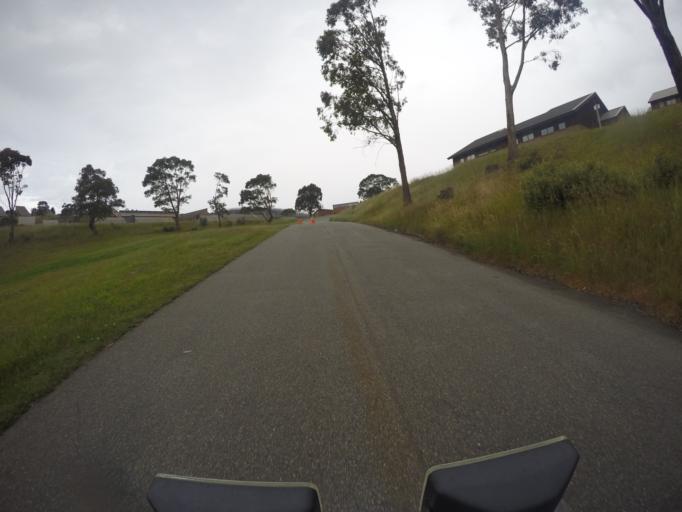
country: AU
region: New South Wales
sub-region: Snowy River
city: Jindabyne
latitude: -35.9351
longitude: 148.3788
